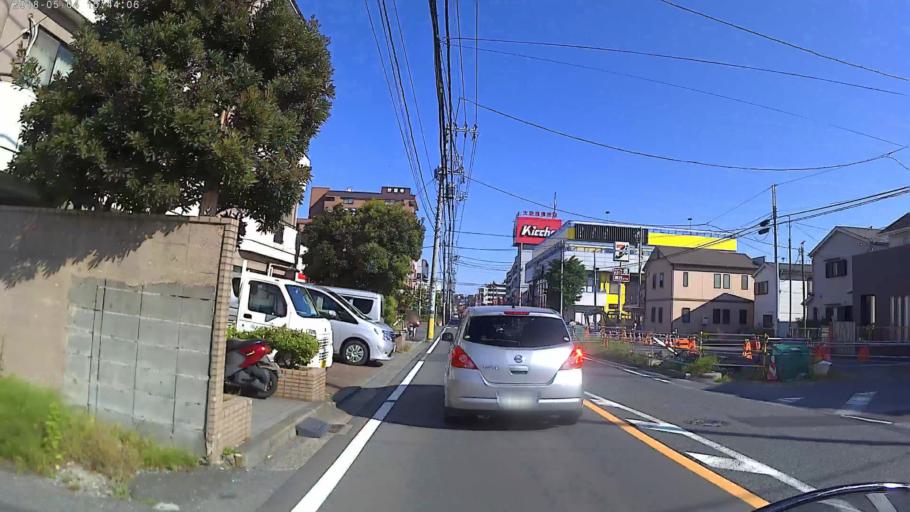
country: JP
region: Kanagawa
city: Yokohama
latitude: 35.5027
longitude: 139.6430
